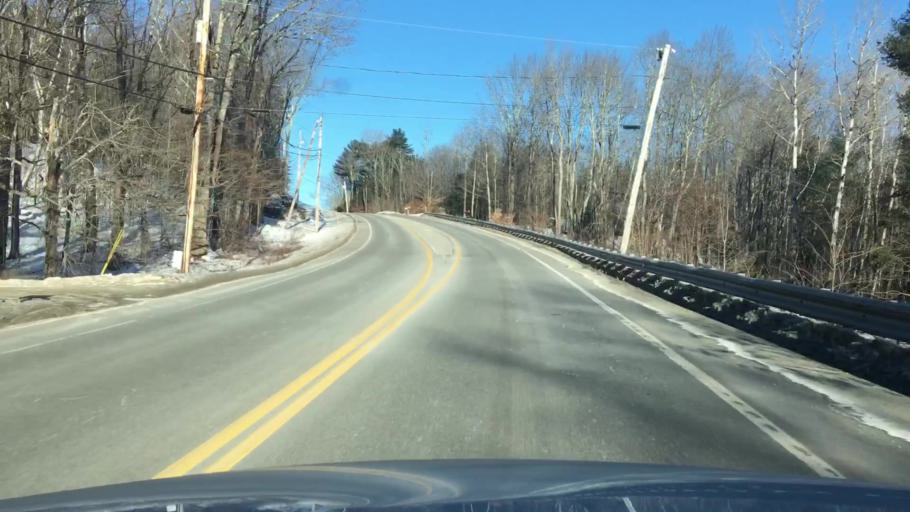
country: US
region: Maine
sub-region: Cumberland County
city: Freeport
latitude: 43.8772
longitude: -70.1075
